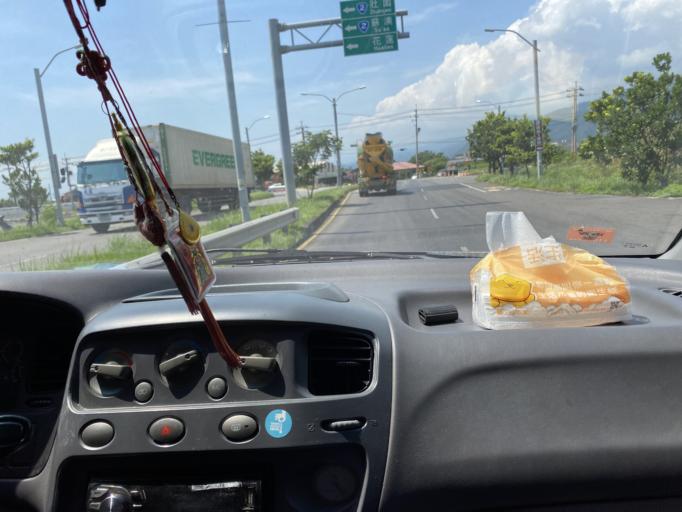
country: TW
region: Taiwan
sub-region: Yilan
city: Yilan
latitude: 24.8475
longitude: 121.8238
